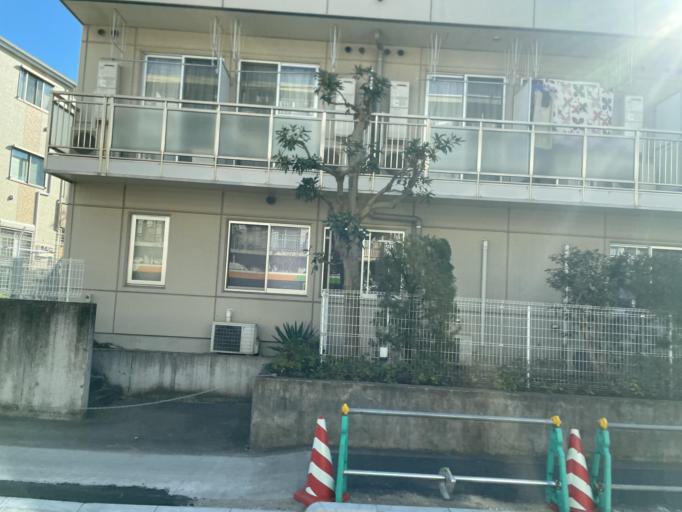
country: JP
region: Tokyo
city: Urayasu
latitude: 35.6640
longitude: 139.8097
